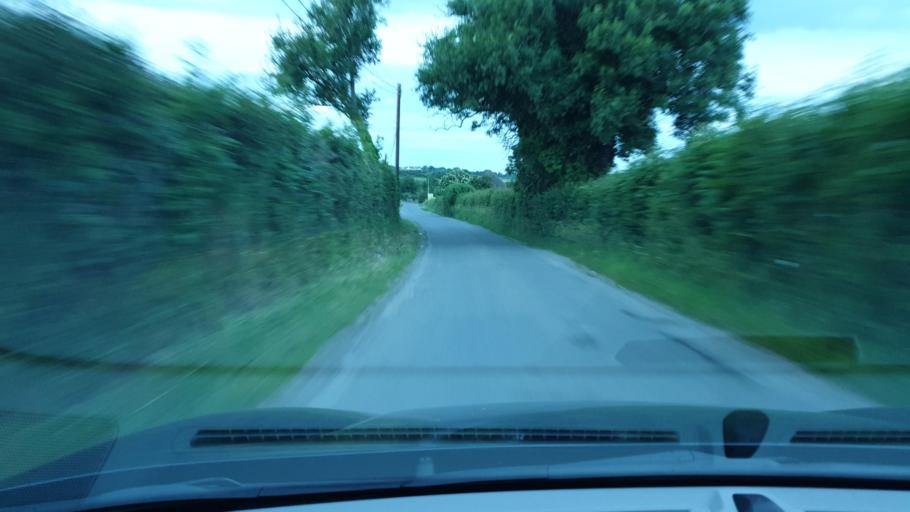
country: IE
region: Leinster
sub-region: An Mhi
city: Duleek
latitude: 53.6055
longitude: -6.3658
